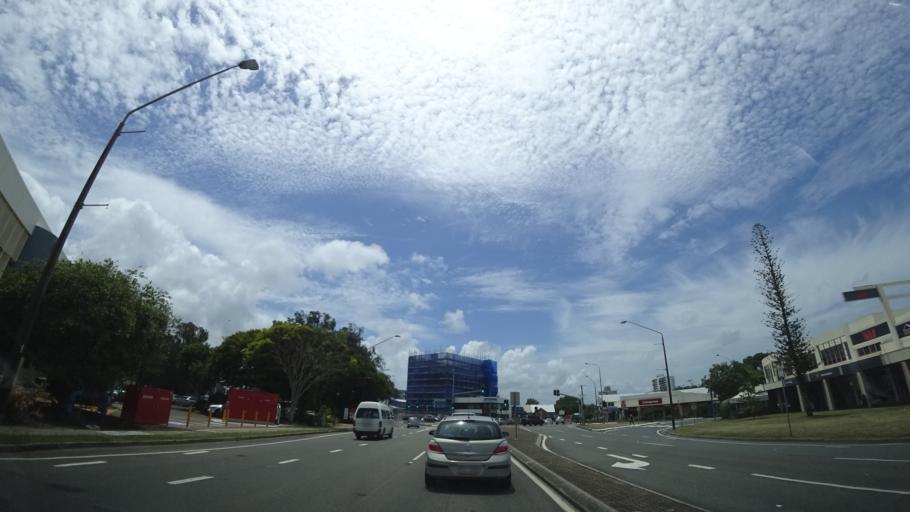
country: AU
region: Queensland
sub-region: Sunshine Coast
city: Mooloolaba
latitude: -26.6535
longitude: 153.0901
